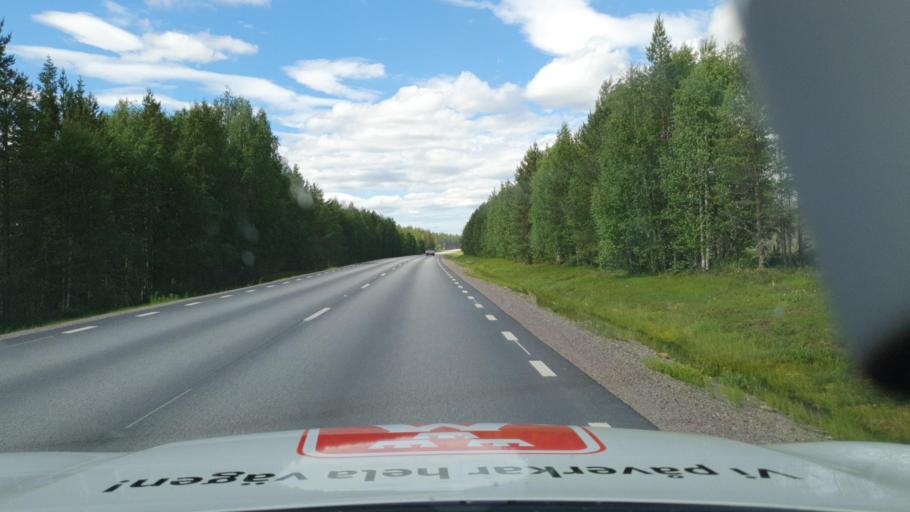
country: SE
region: Vaesterbotten
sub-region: Skelleftea Kommun
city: Langsele
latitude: 65.0715
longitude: 20.0249
